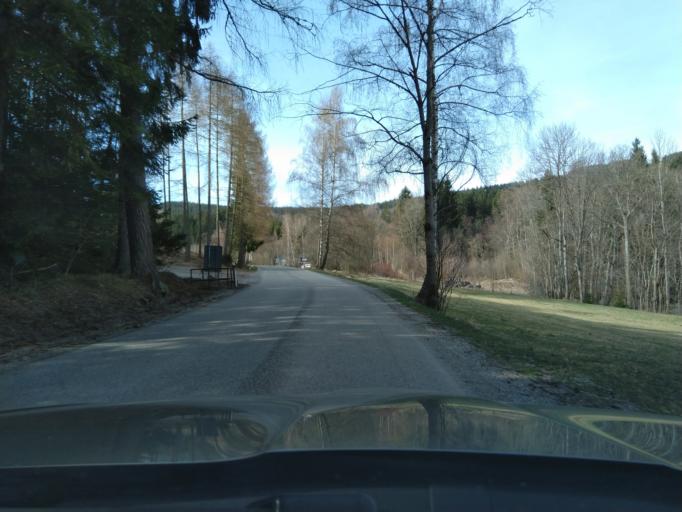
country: CZ
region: Jihocesky
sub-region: Okres Prachatice
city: Stachy
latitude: 49.0740
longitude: 13.6359
